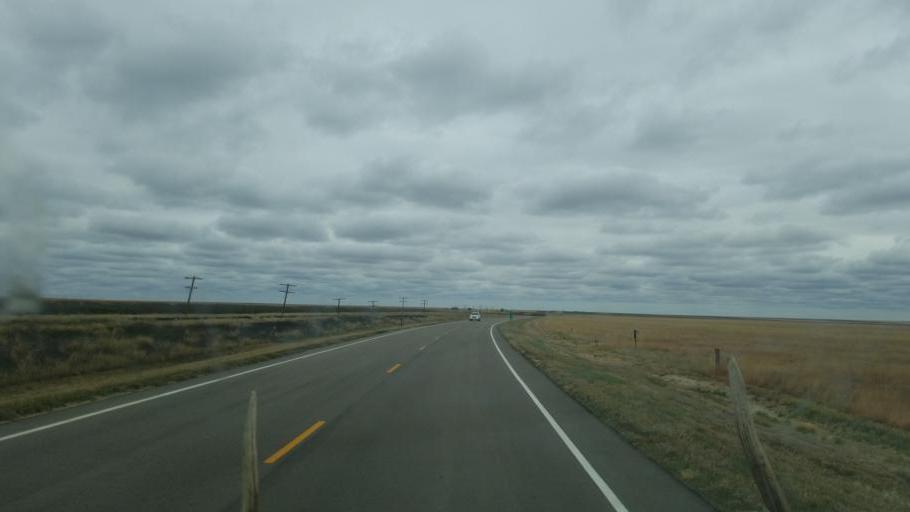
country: US
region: Colorado
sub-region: Kiowa County
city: Eads
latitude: 38.5049
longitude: -103.0435
